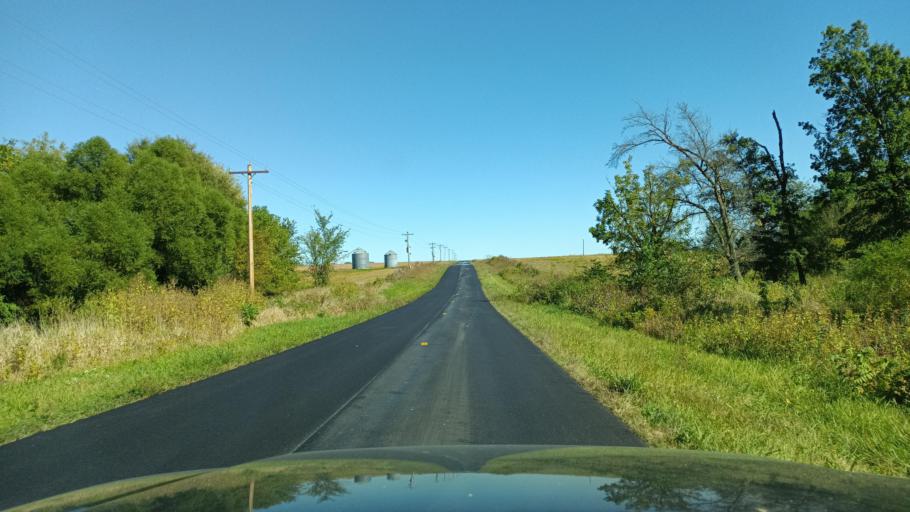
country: US
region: Missouri
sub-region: Macon County
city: La Plata
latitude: 39.9278
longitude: -92.5636
